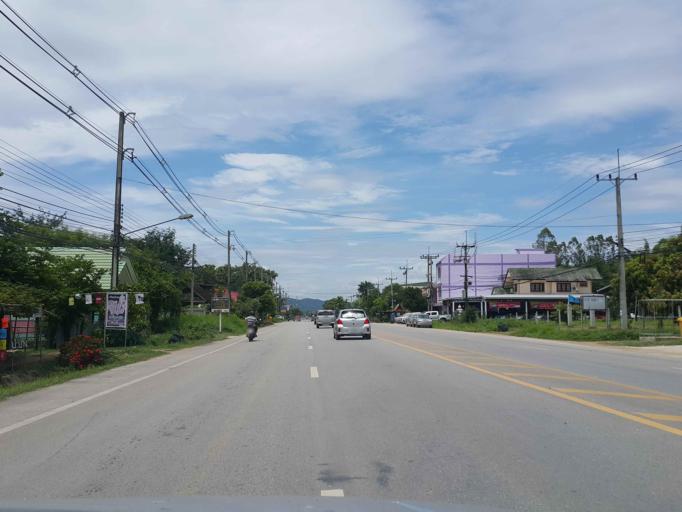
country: TH
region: Sukhothai
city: Ban Na
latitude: 17.0150
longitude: 99.7459
